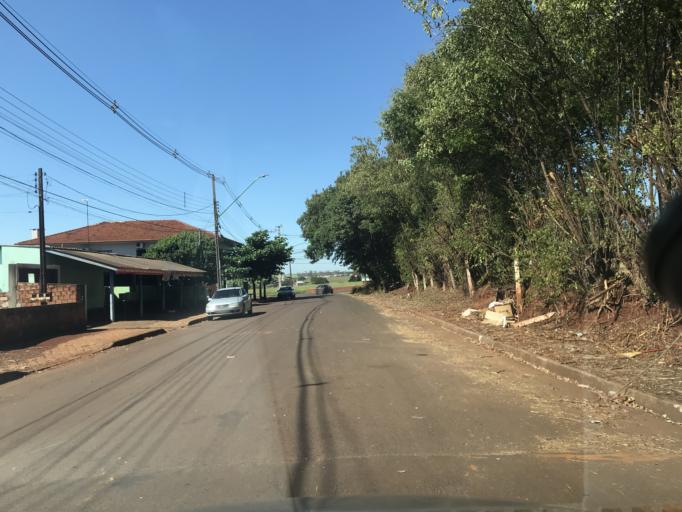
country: BR
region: Parana
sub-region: Palotina
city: Palotina
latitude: -24.2791
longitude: -53.8278
